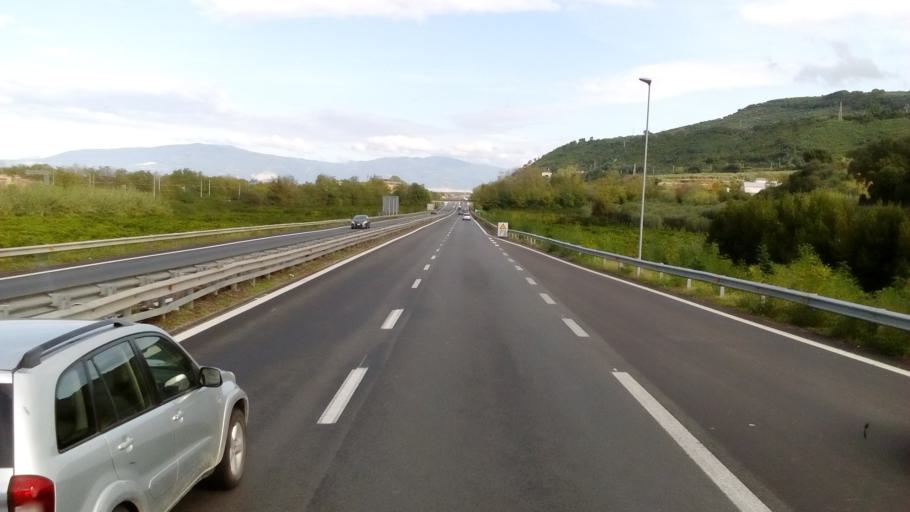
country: IT
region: Calabria
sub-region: Provincia di Vibo-Valentia
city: Pizzo
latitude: 38.7734
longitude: 16.2144
